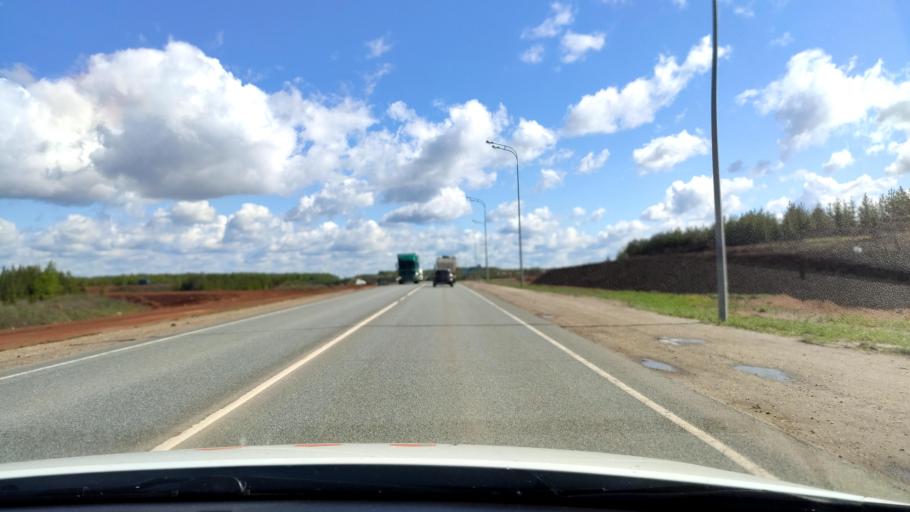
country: RU
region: Tatarstan
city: Sviyazhsk
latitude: 55.7344
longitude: 48.7783
